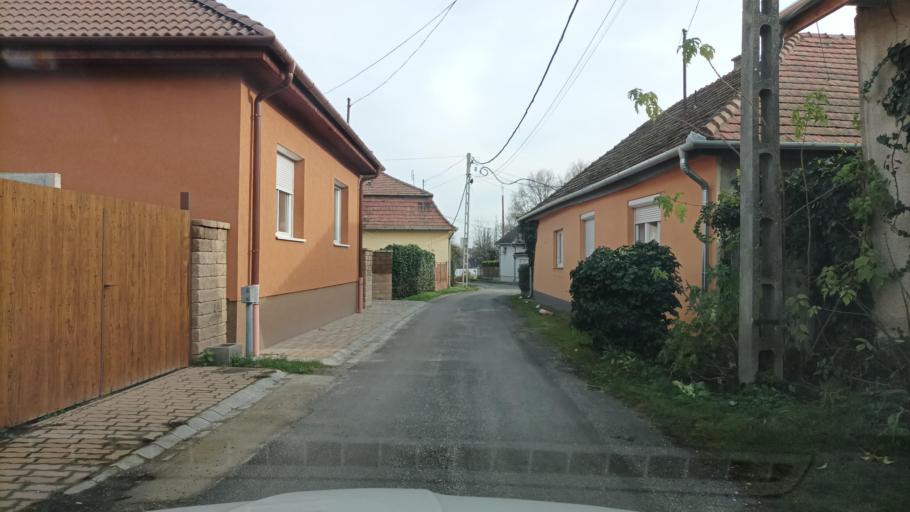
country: HU
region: Pest
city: Rackeve
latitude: 47.1553
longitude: 18.9452
